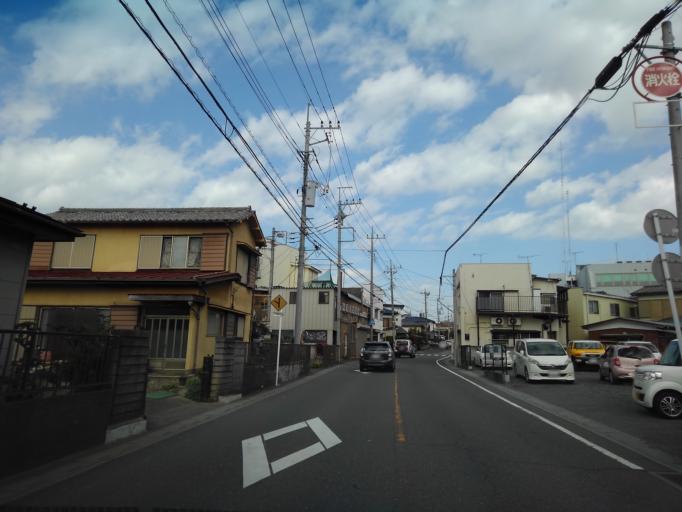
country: JP
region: Tokyo
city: Higashimurayama-shi
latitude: 35.7756
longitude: 139.4724
